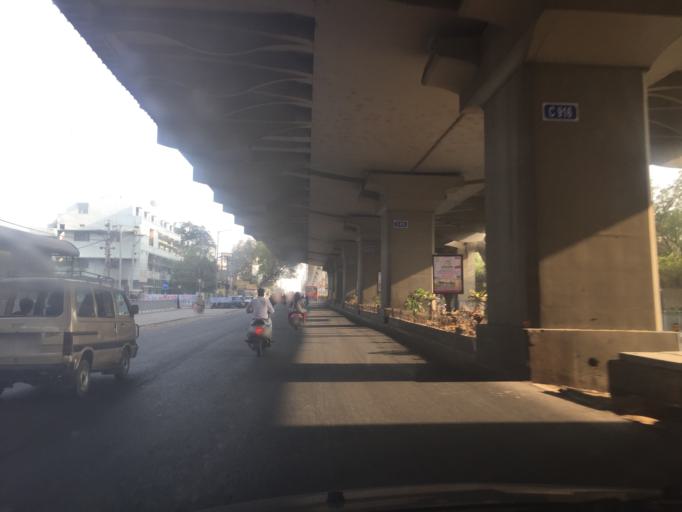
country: IN
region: Telangana
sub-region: Rangareddi
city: Uppal Kalan
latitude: 17.4077
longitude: 78.5540
